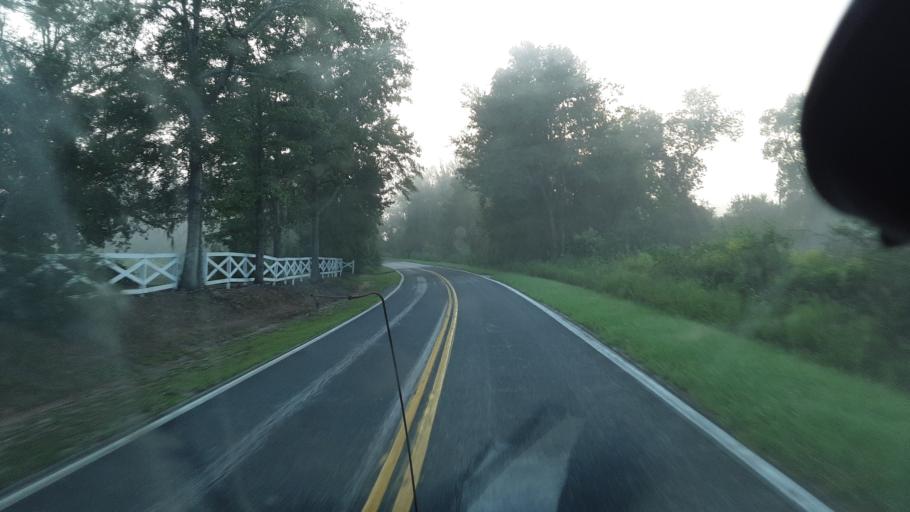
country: US
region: South Carolina
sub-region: Clarendon County
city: Manning
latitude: 33.7309
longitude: -80.0948
